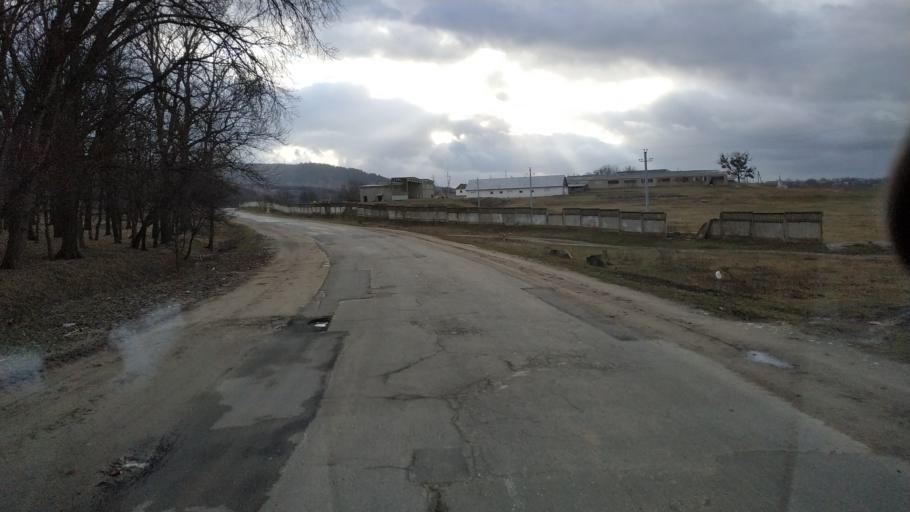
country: MD
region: Calarasi
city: Calarasi
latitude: 47.3090
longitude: 28.3694
